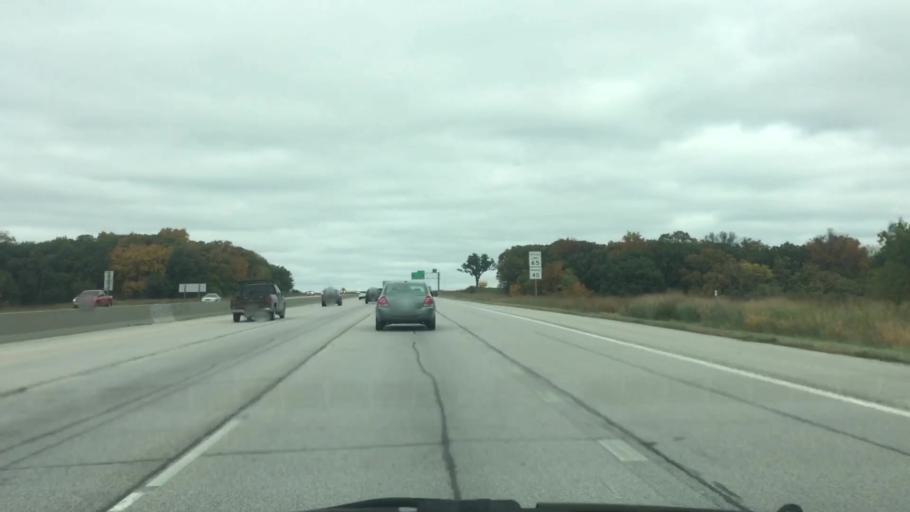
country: US
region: Iowa
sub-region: Polk County
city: Clive
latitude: 41.6205
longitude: -93.7767
